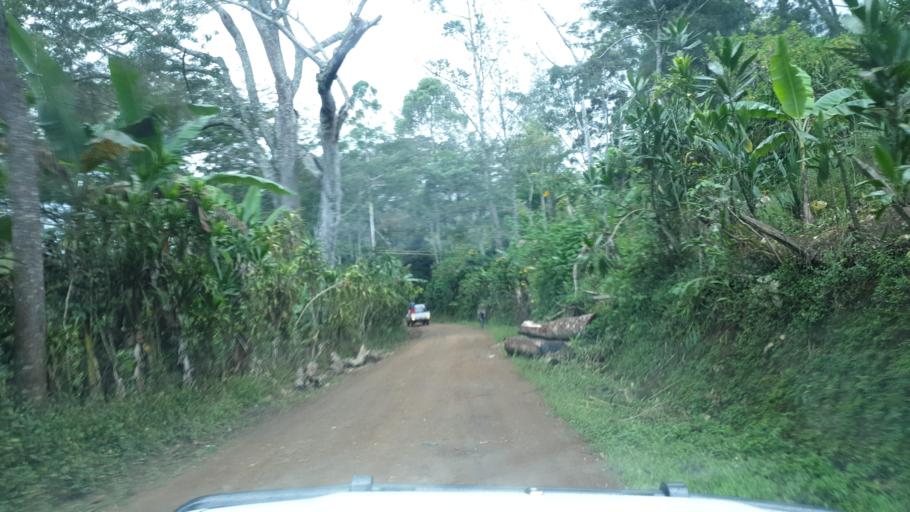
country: PG
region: Eastern Highlands
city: Goroka
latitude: -5.9703
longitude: 145.2769
